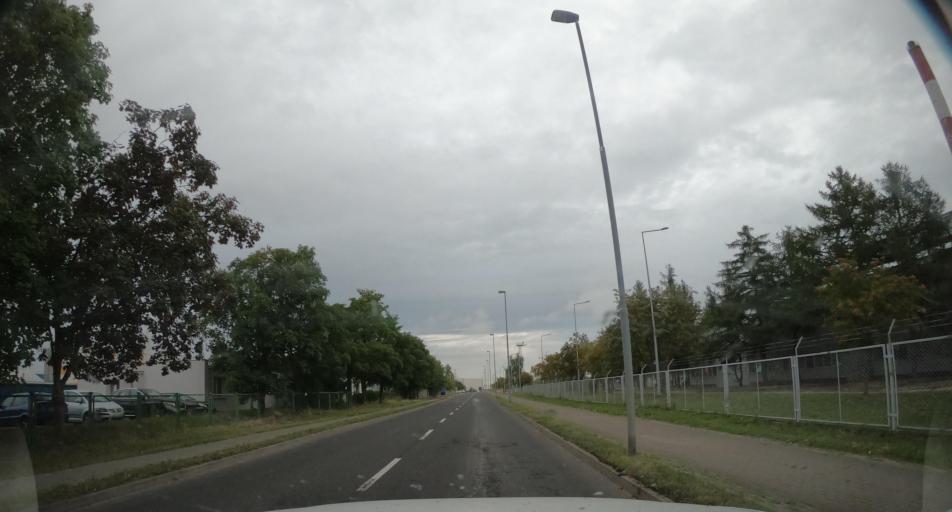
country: PL
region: West Pomeranian Voivodeship
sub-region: Powiat stargardzki
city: Stargard Szczecinski
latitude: 53.3499
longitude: 15.0040
